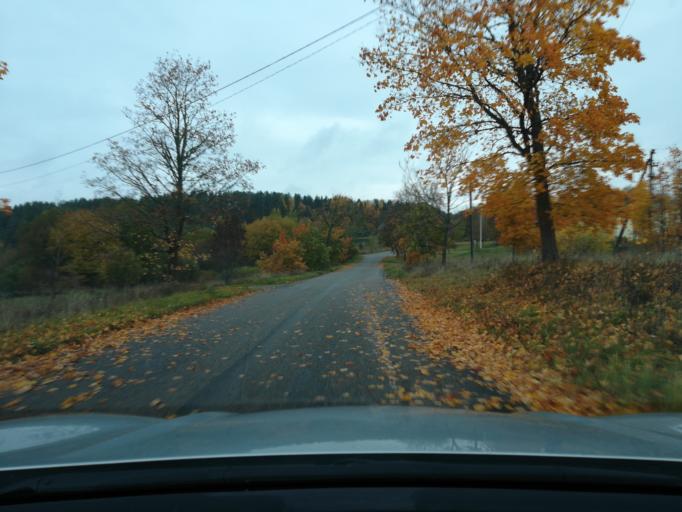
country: EE
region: Ida-Virumaa
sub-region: Johvi vald
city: Johvi
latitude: 59.1925
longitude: 27.5438
